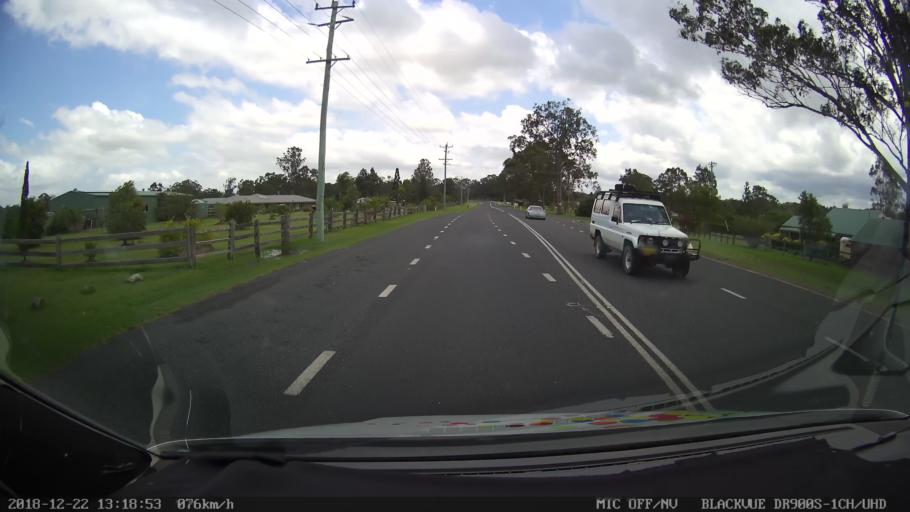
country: AU
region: New South Wales
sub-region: Clarence Valley
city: South Grafton
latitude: -29.7512
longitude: 152.9318
